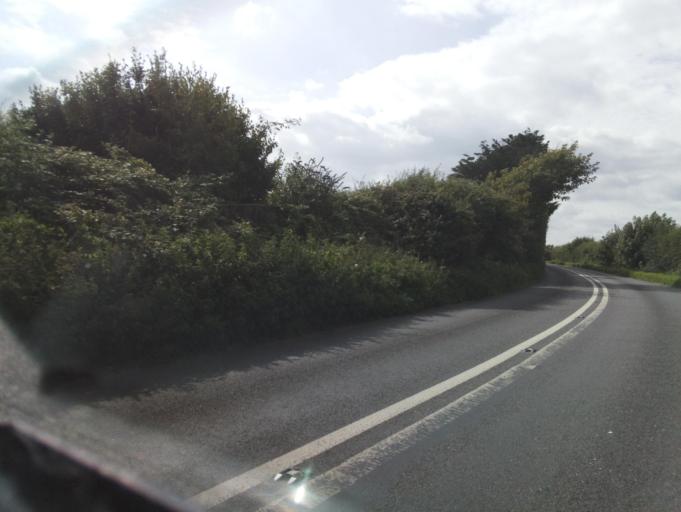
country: GB
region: England
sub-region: Hampshire
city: Milford on Sea
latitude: 50.7305
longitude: -1.6183
